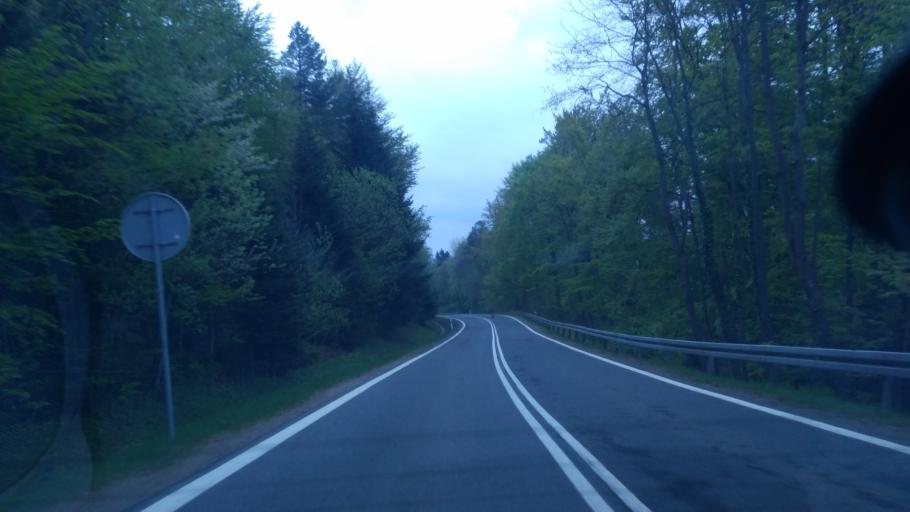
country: PL
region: Subcarpathian Voivodeship
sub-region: Powiat sanocki
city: Tyrawa Woloska
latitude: 49.5584
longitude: 22.3374
